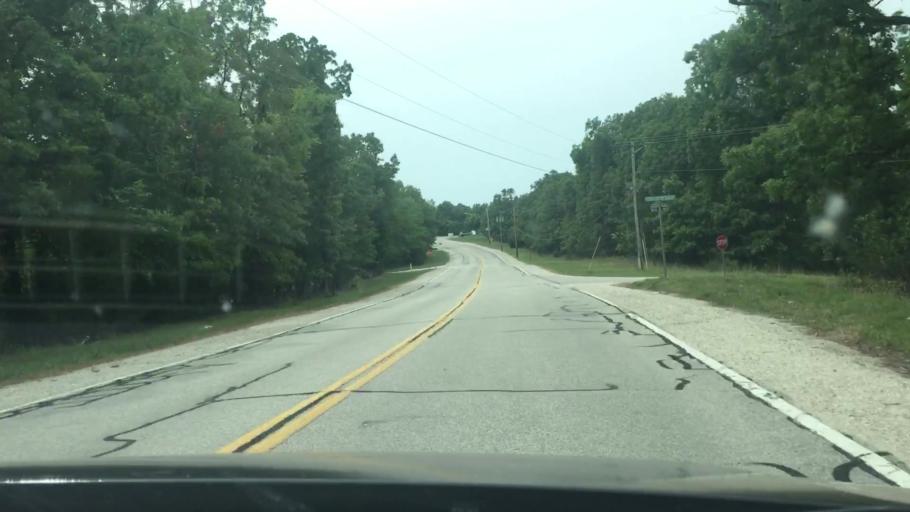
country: US
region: Missouri
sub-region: Camden County
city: Four Seasons
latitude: 38.2040
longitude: -92.7025
